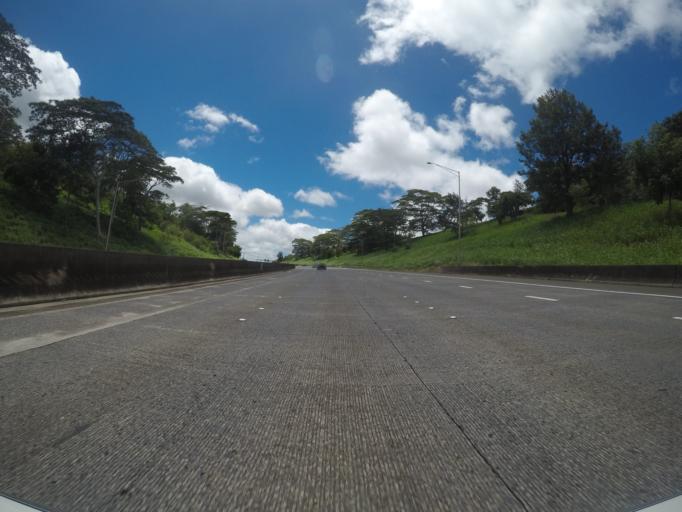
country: US
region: Hawaii
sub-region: Honolulu County
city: Mililani Town
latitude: 21.4607
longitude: -157.9953
